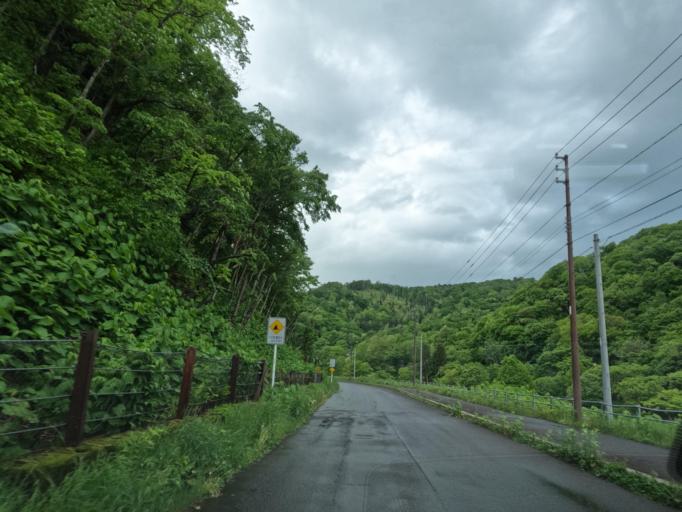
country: JP
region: Hokkaido
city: Fukagawa
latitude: 43.7303
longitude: 142.2031
